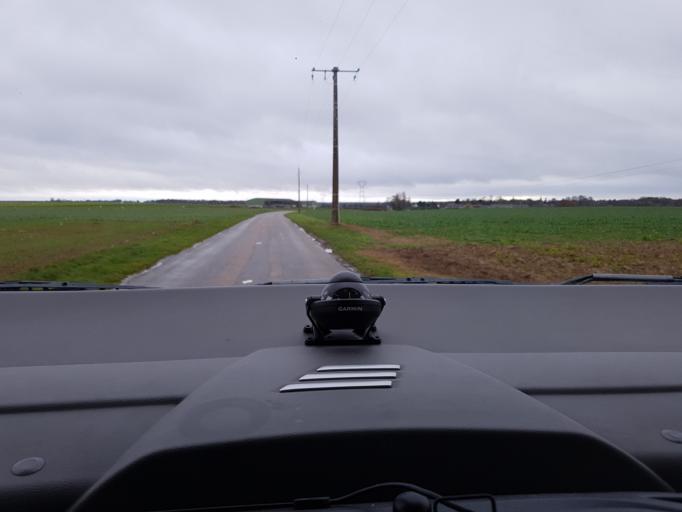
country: FR
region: Haute-Normandie
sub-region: Departement de l'Eure
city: Pont-Saint-Pierre
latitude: 49.2963
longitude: 1.3320
